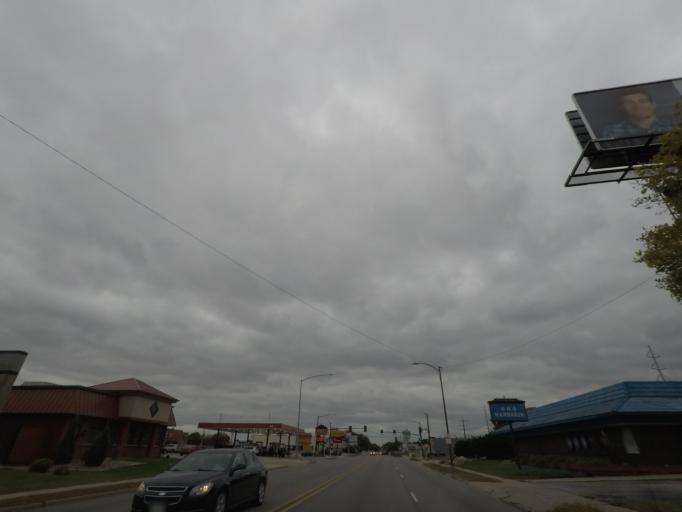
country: US
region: Iowa
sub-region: Story County
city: Ames
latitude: 42.0229
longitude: -93.6156
